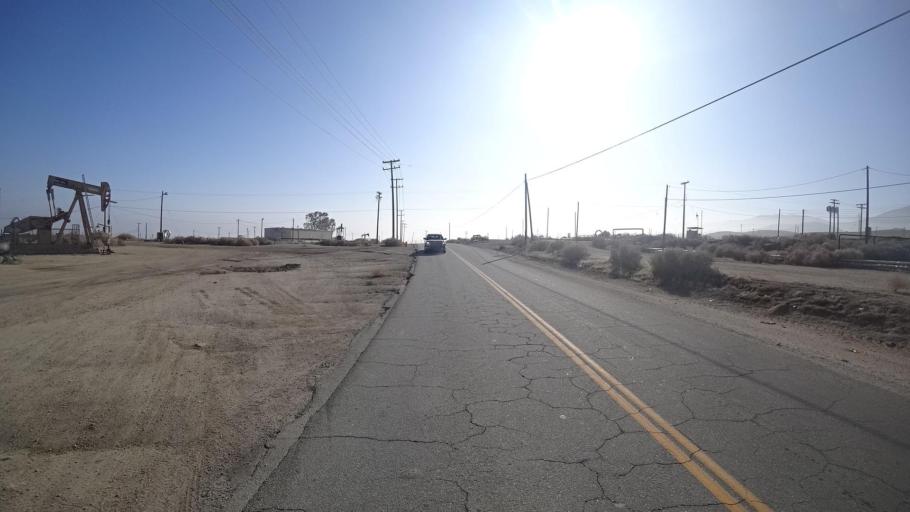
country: US
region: California
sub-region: Kern County
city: Taft Heights
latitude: 35.2036
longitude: -119.5953
